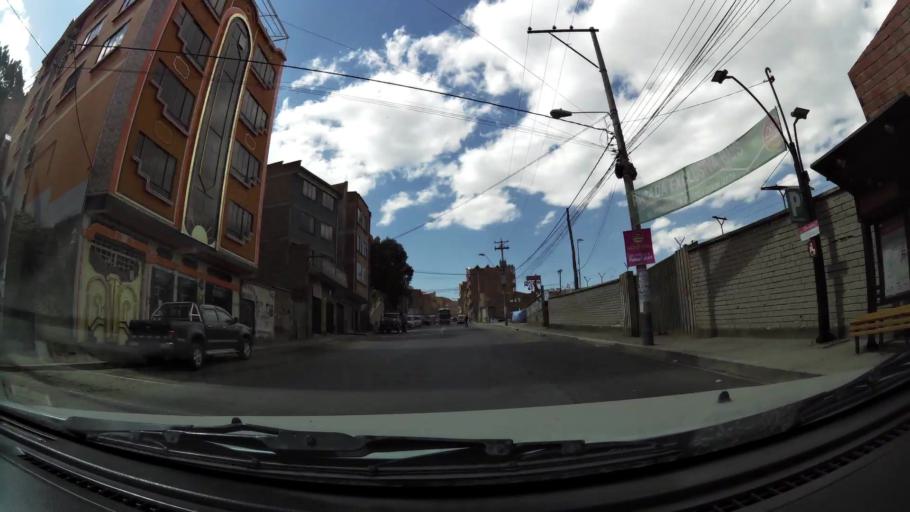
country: BO
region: La Paz
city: La Paz
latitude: -16.4642
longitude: -68.1091
